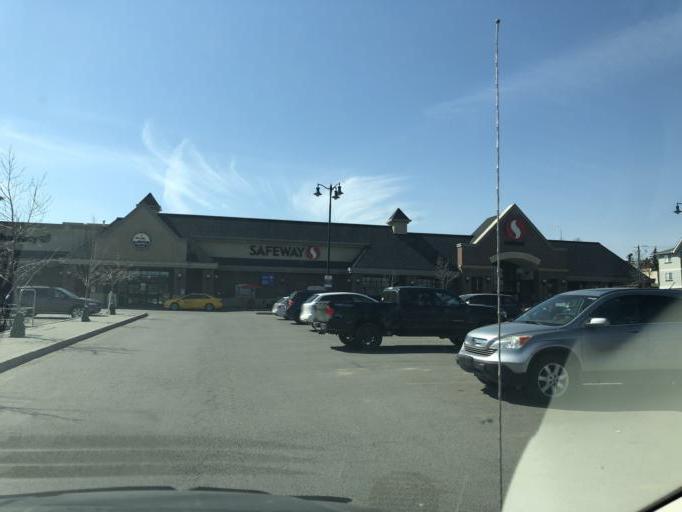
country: CA
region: Alberta
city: Calgary
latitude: 51.0226
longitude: -114.1154
